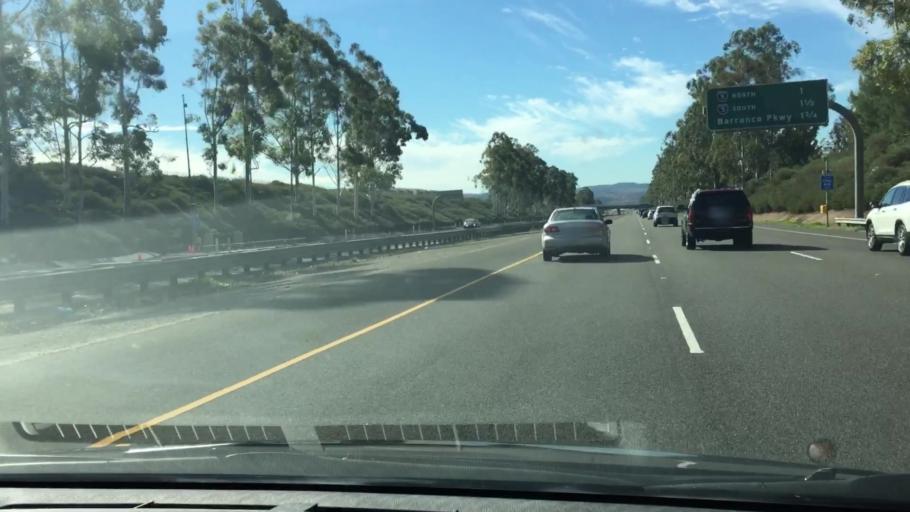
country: US
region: California
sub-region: Orange County
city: Lake Forest
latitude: 33.6907
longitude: -117.7411
